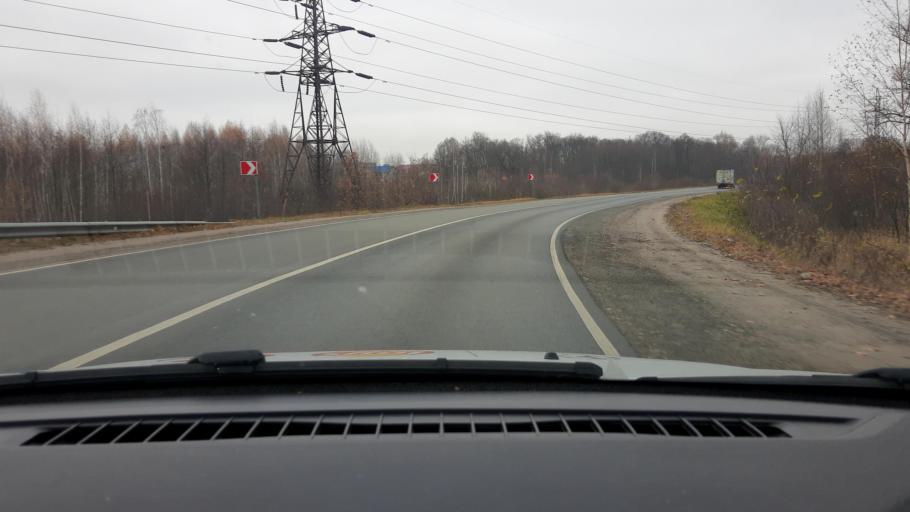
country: RU
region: Nizjnij Novgorod
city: Novaya Balakhna
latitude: 56.5141
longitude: 43.5780
